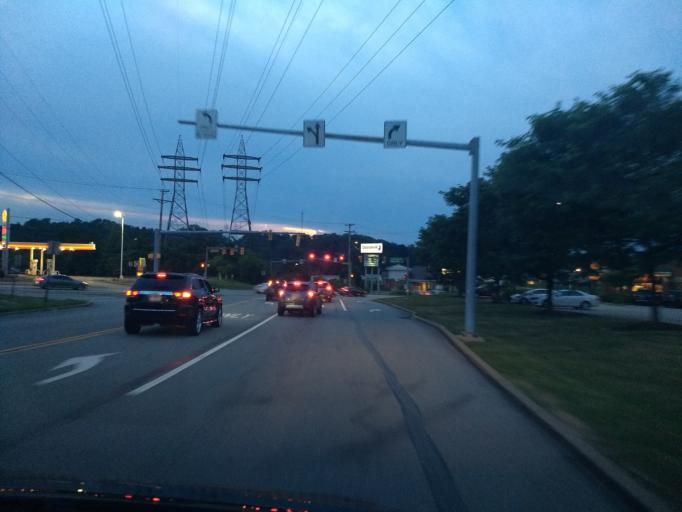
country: US
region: Pennsylvania
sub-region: Allegheny County
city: Wilmerding
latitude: 40.3849
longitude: -79.8235
